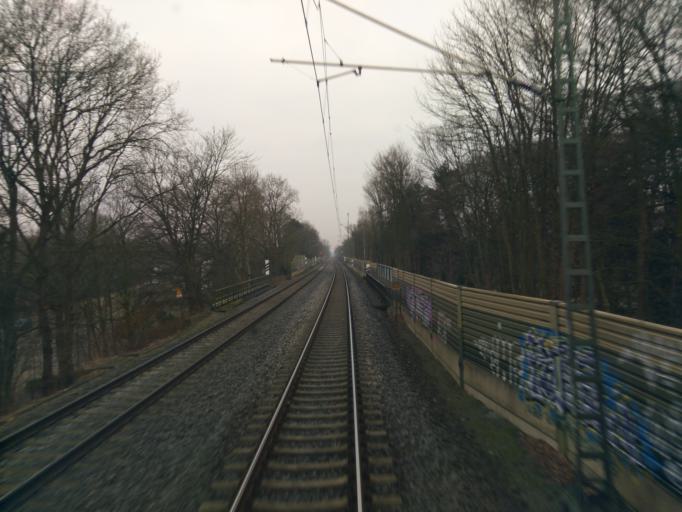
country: DE
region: Lower Saxony
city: Lilienthal
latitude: 53.0972
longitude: 8.8824
